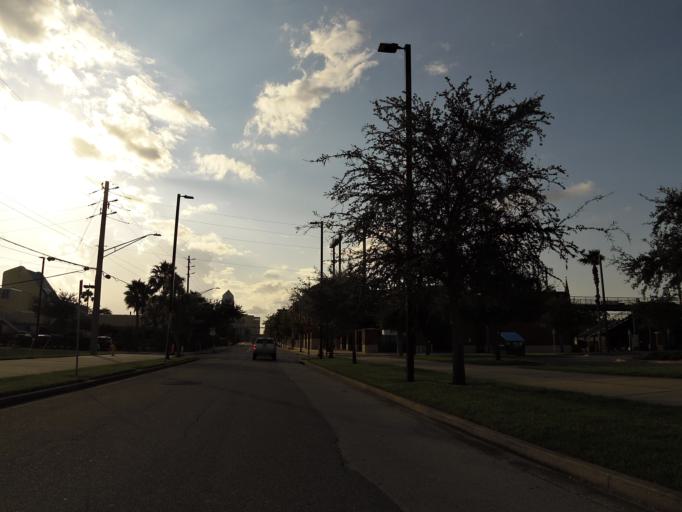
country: US
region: Florida
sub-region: Duval County
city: Jacksonville
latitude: 30.3239
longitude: -81.6416
